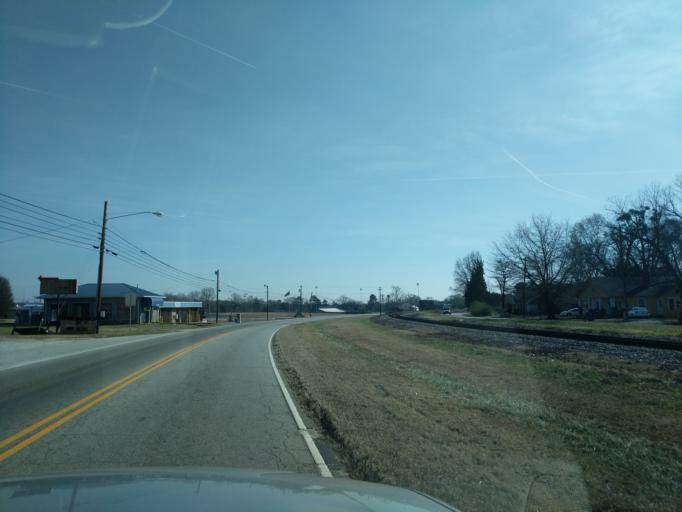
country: US
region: South Carolina
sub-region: Spartanburg County
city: Woodruff
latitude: 34.7339
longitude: -82.0301
